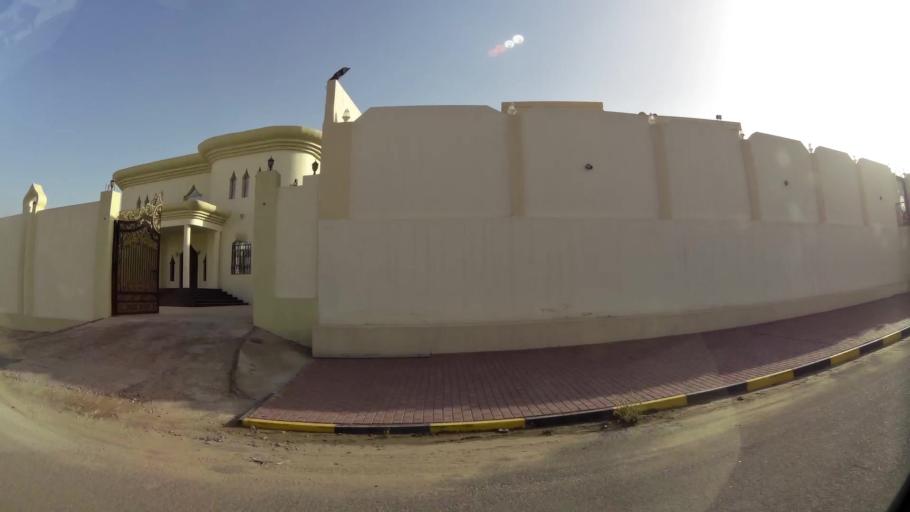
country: QA
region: Baladiyat ar Rayyan
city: Ar Rayyan
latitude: 25.3359
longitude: 51.4332
